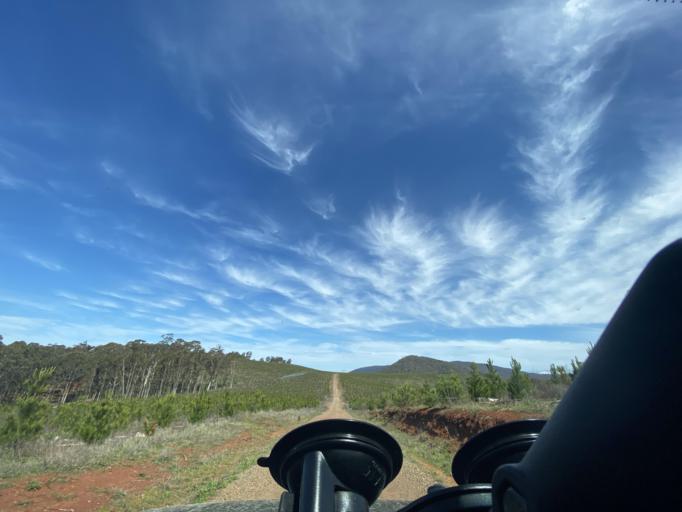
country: AU
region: Victoria
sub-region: Mansfield
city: Mansfield
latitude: -36.8183
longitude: 146.1020
